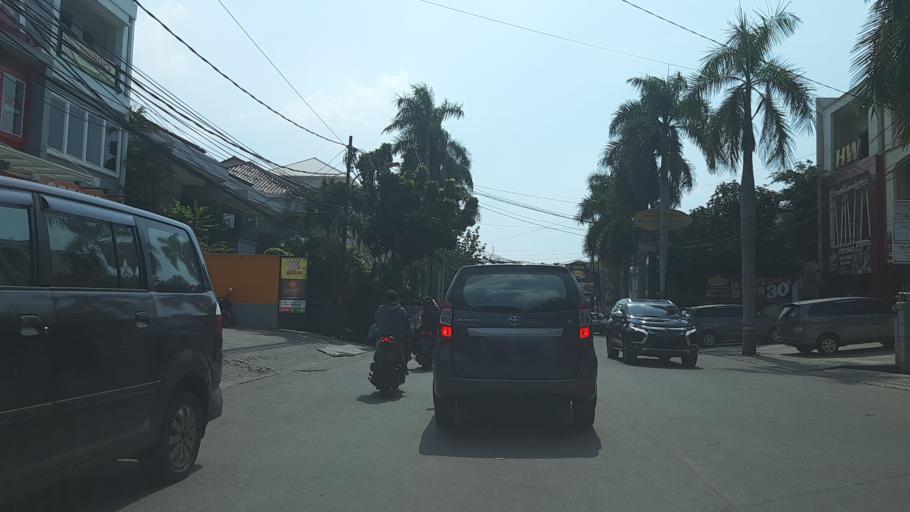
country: ID
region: Jakarta Raya
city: Jakarta
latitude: -6.1696
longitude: 106.7707
